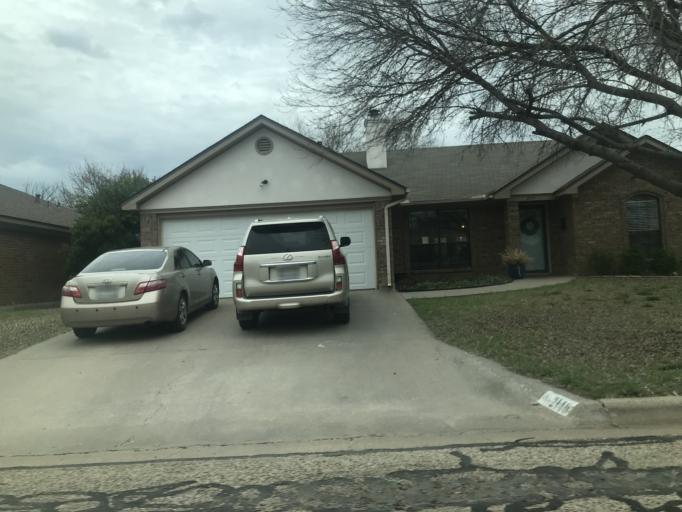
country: US
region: Texas
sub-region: Taylor County
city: Abilene
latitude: 32.4880
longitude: -99.6878
